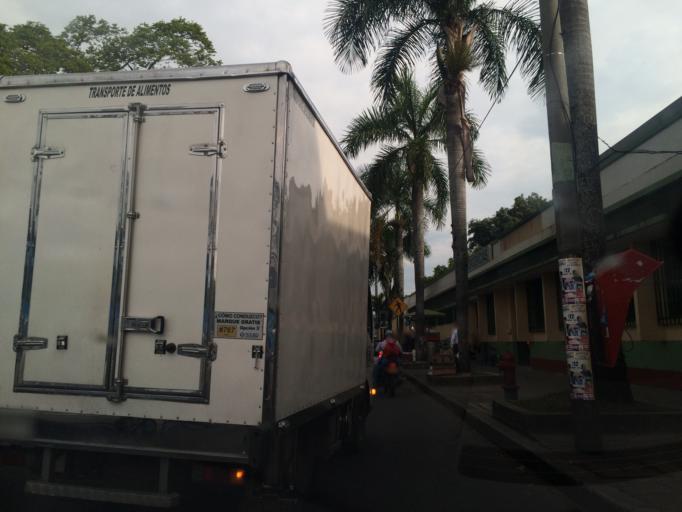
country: CO
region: Valle del Cauca
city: Cali
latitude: 3.3877
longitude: -76.5451
